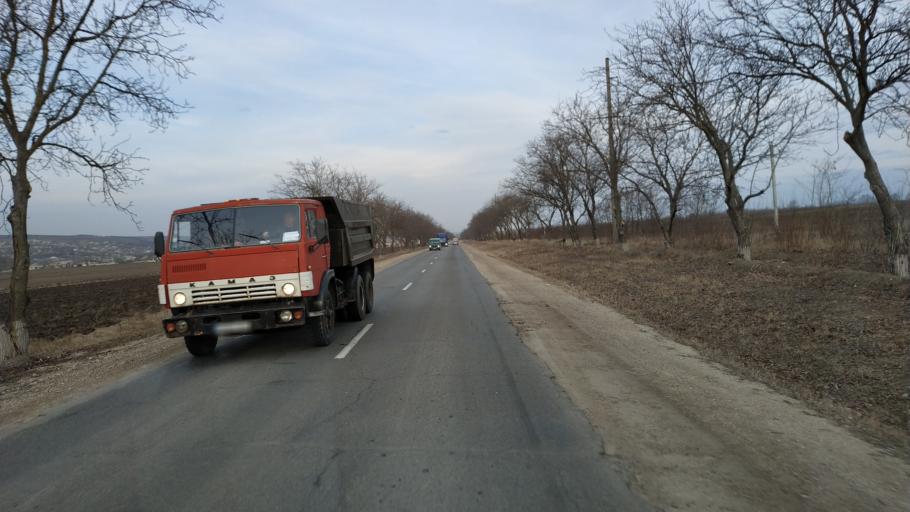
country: MD
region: Laloveni
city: Ialoveni
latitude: 46.9342
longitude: 28.8074
